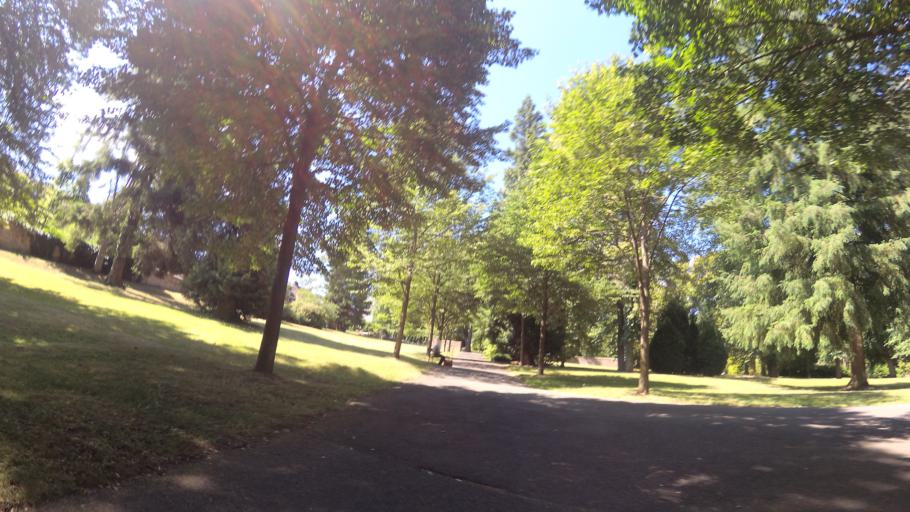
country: DE
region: Saarland
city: Neunkirchen
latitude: 49.3341
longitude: 7.1828
